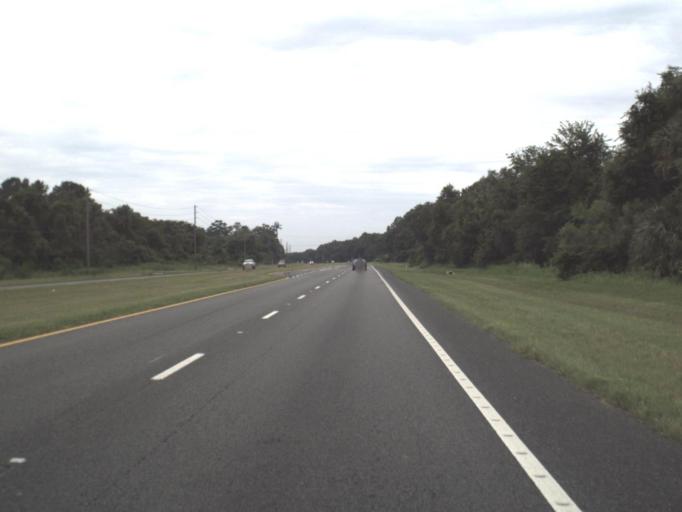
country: US
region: Florida
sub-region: Citrus County
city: Inverness
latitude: 28.8512
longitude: -82.2336
